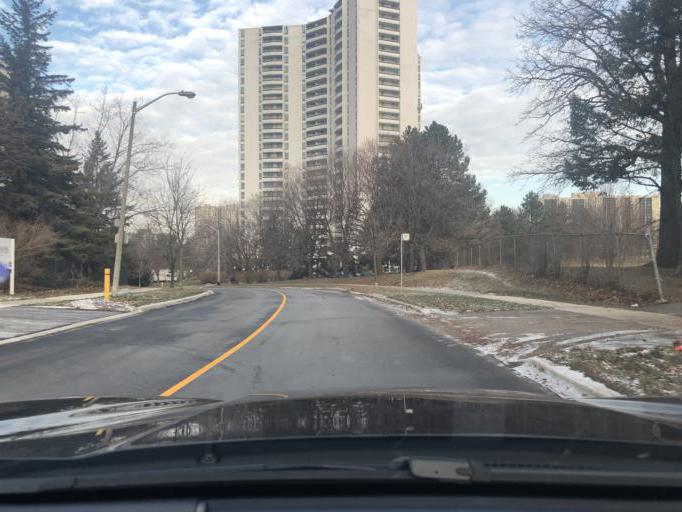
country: CA
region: Ontario
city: Willowdale
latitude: 43.7642
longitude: -79.3422
